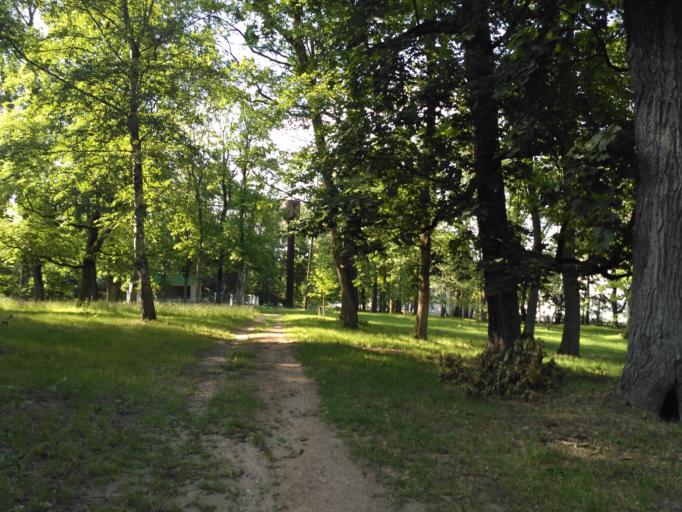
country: BY
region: Minsk
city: Chervyen'
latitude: 53.8845
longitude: 28.6157
